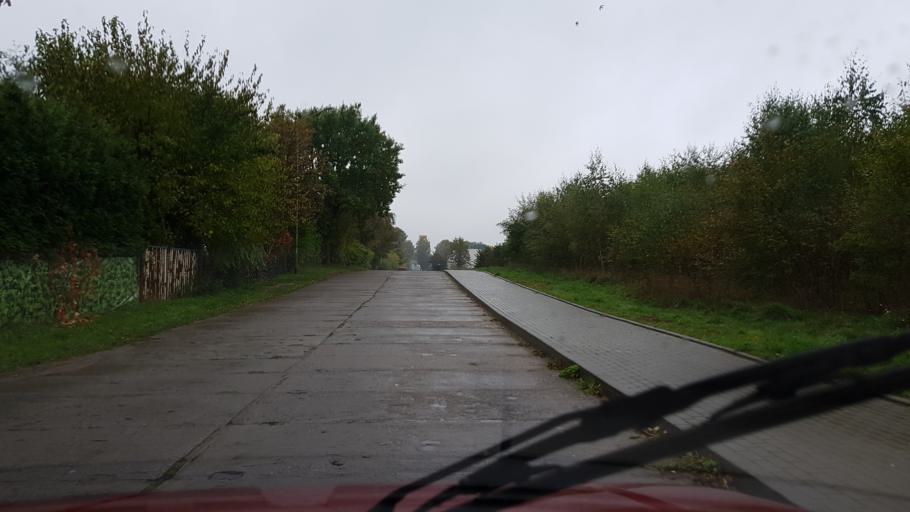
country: PL
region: West Pomeranian Voivodeship
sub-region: Powiat drawski
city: Czaplinek
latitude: 53.5491
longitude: 16.2408
